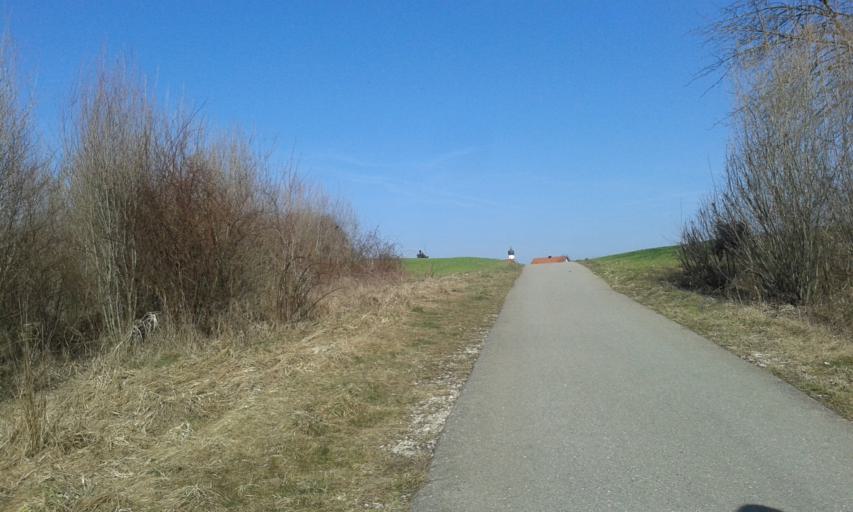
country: DE
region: Baden-Wuerttemberg
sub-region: Tuebingen Region
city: Ehingen
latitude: 48.2952
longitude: 9.7246
